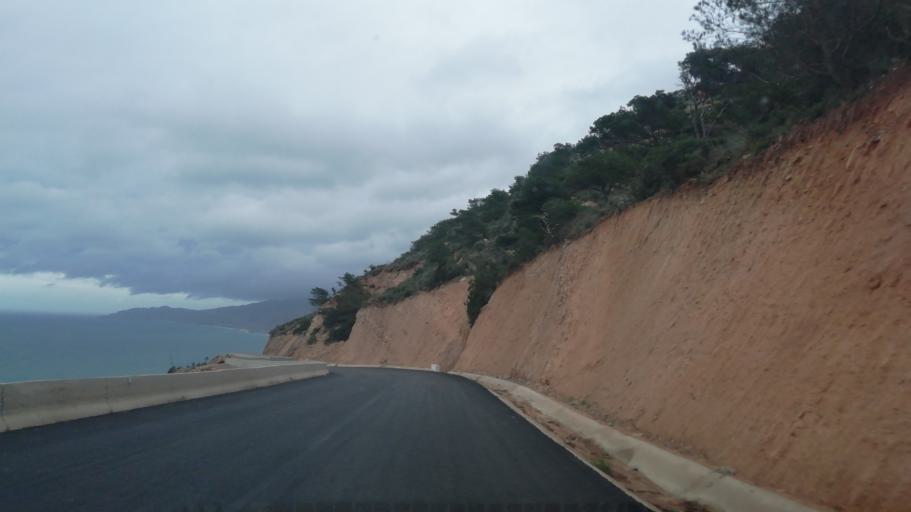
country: DZ
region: Oran
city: Bir el Djir
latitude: 35.7625
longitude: -0.5278
